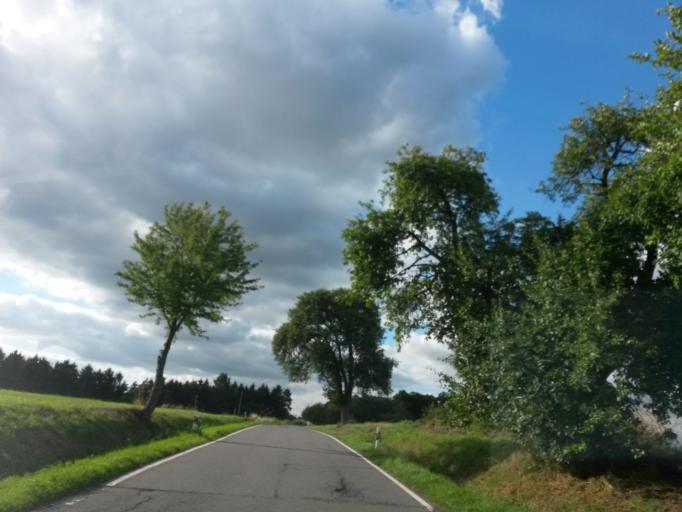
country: DE
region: North Rhine-Westphalia
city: Waldbrol
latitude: 50.9038
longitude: 7.6253
